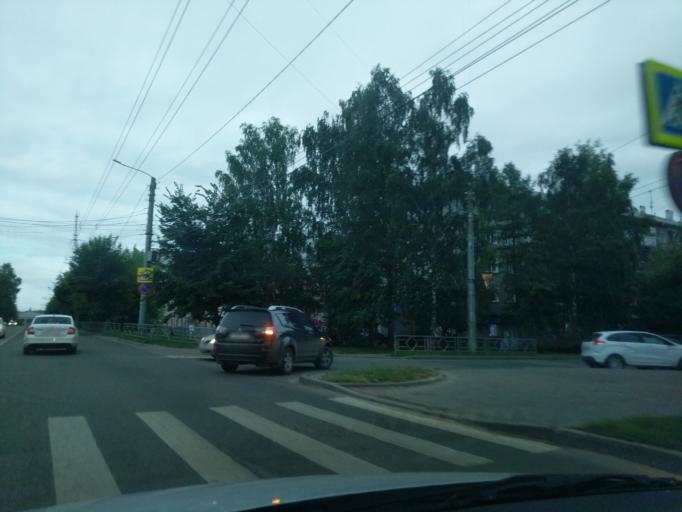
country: RU
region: Kirov
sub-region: Kirovo-Chepetskiy Rayon
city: Kirov
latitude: 58.5940
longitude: 49.6730
